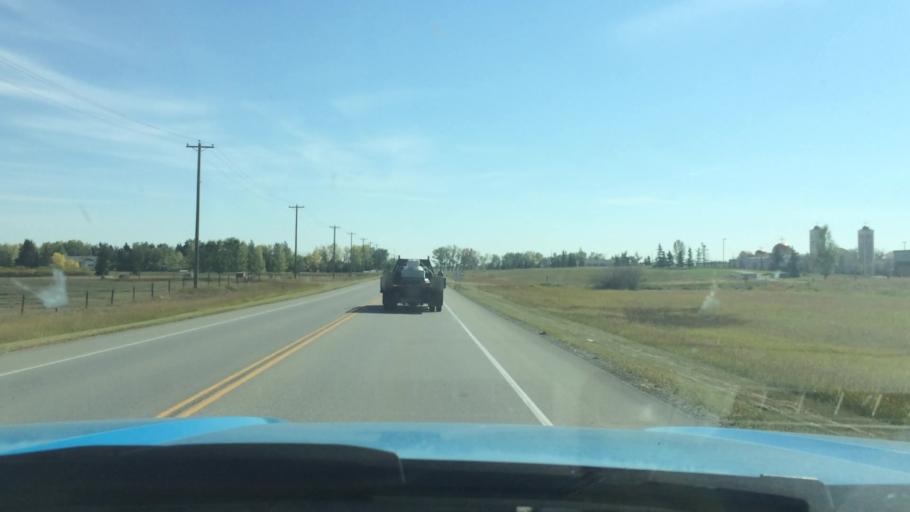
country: CA
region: Alberta
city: Airdrie
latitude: 51.2127
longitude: -113.9719
